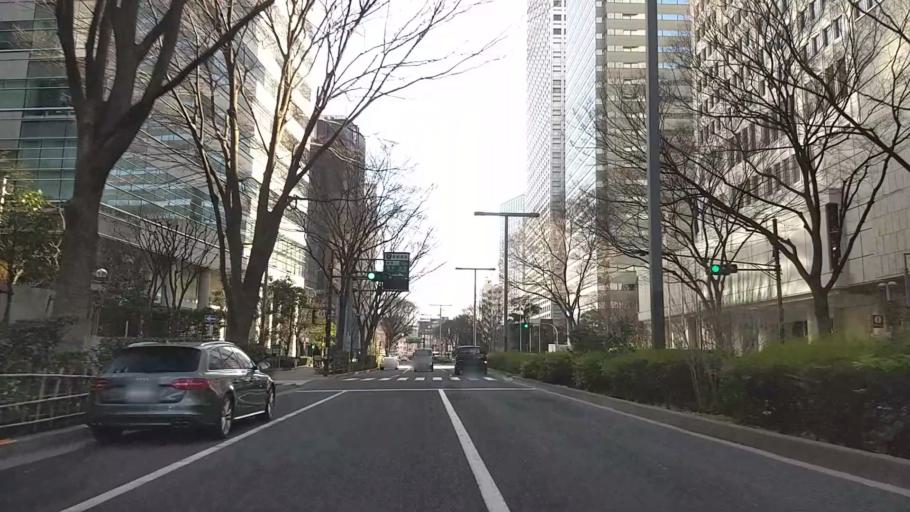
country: JP
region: Tokyo
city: Tokyo
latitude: 35.6903
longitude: 139.6949
